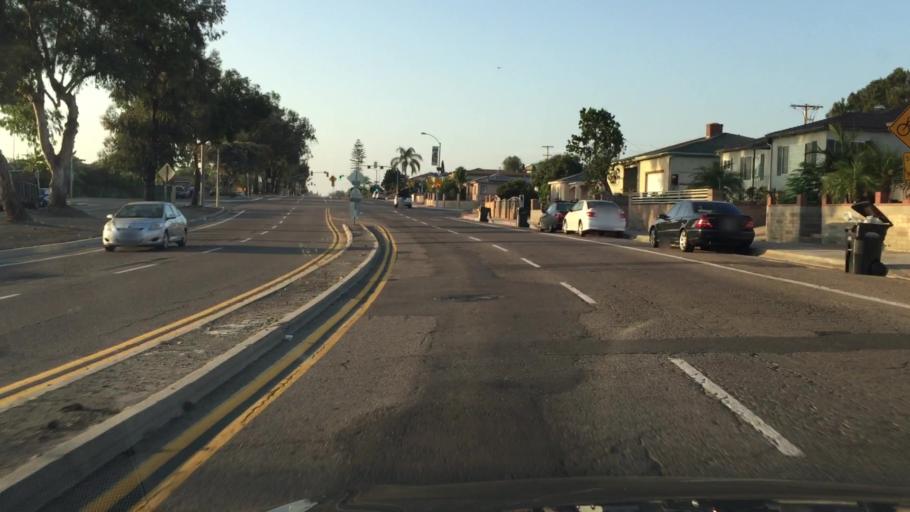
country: US
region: California
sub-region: San Diego County
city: Lemon Grove
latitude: 32.7299
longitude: -117.0798
